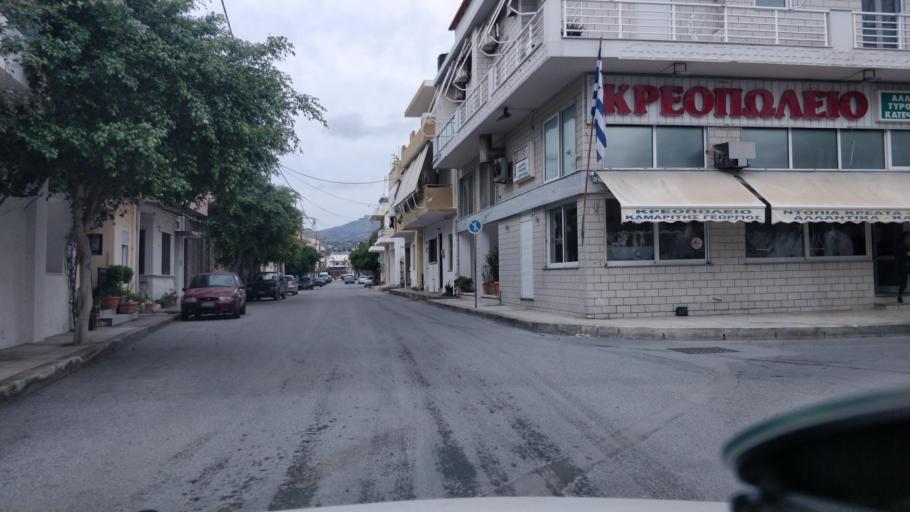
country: GR
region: Crete
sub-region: Nomos Lasithiou
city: Ierapetra
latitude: 35.0055
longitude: 25.7353
